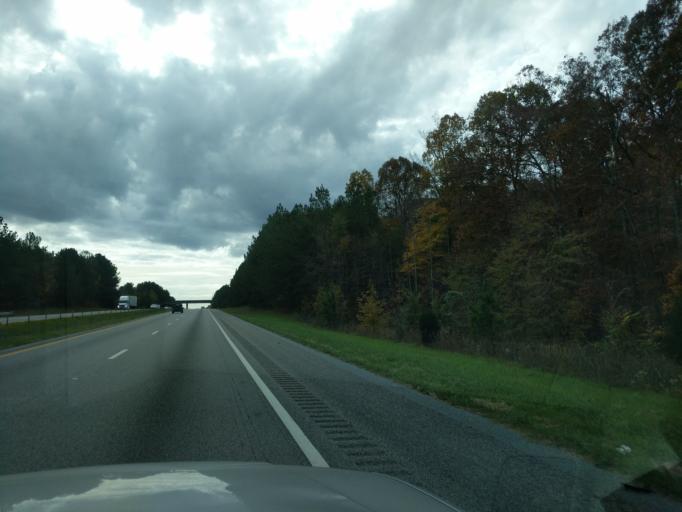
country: US
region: South Carolina
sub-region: Laurens County
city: Clinton
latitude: 34.5674
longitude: -81.8920
